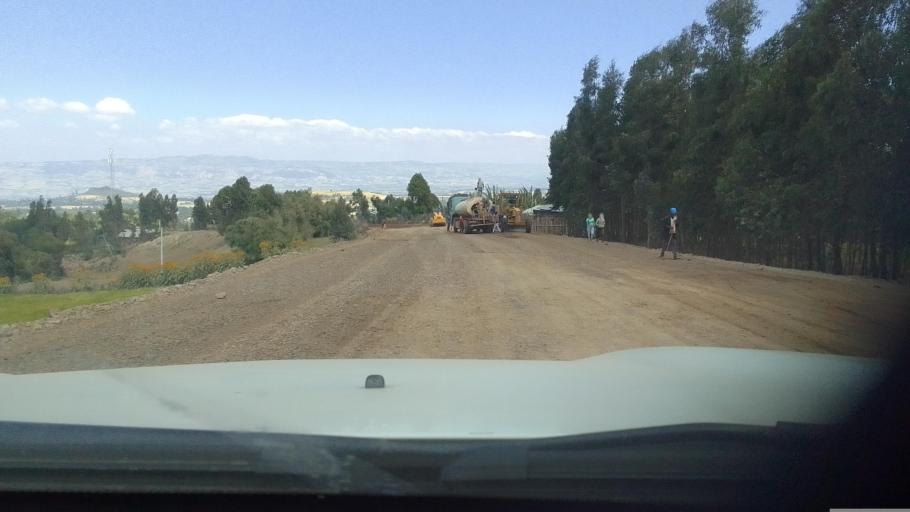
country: ET
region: Oromiya
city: Hagere Hiywet
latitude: 8.8514
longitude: 37.8927
